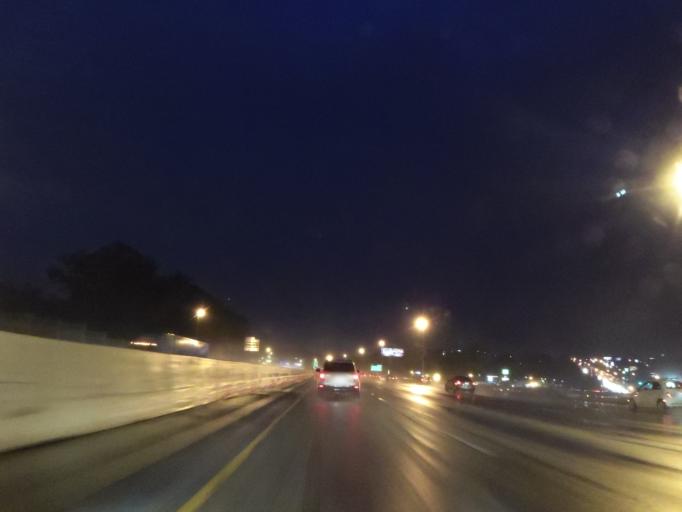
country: US
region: Tennessee
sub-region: Knox County
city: Knoxville
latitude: 35.9334
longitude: -84.0211
